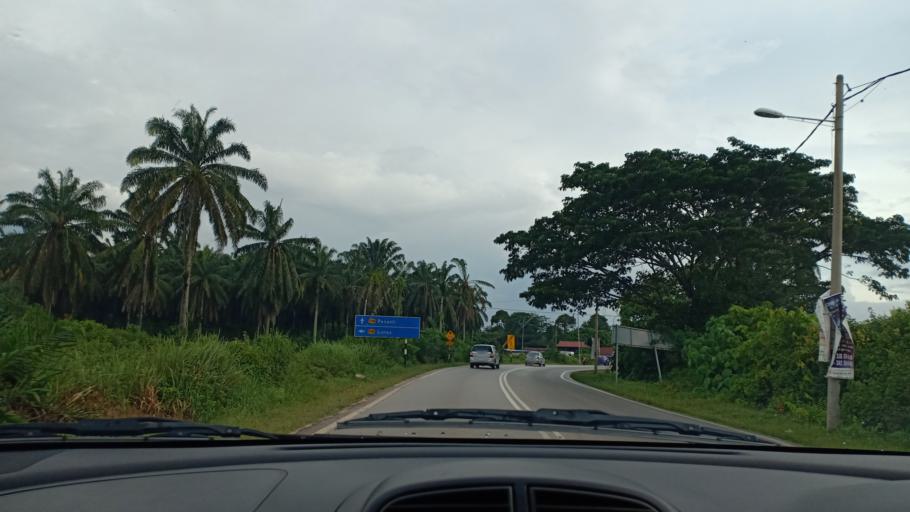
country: MY
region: Penang
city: Tasek Glugor
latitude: 5.4398
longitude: 100.5131
